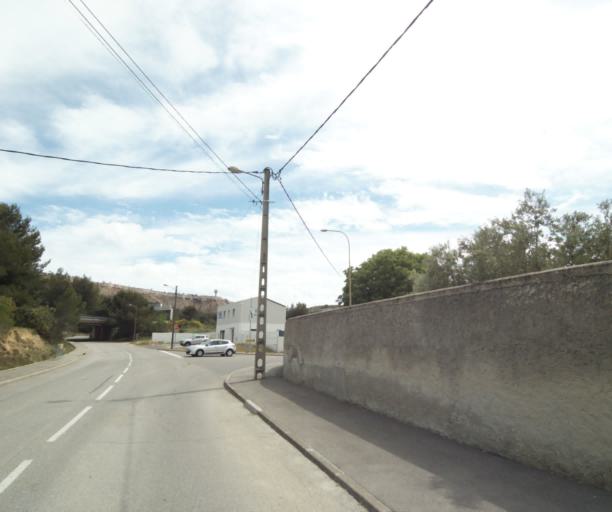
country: FR
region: Provence-Alpes-Cote d'Azur
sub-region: Departement des Bouches-du-Rhone
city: Rognac
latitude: 43.4807
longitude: 5.2390
